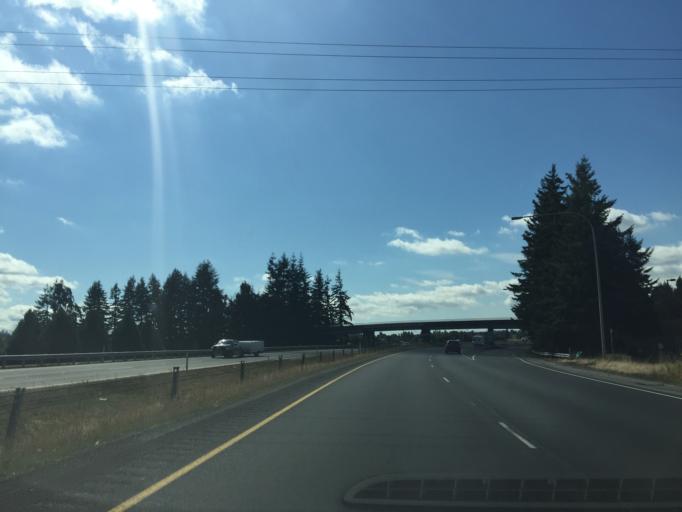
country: US
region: Washington
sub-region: Skagit County
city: Burlington
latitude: 48.4865
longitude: -122.3362
